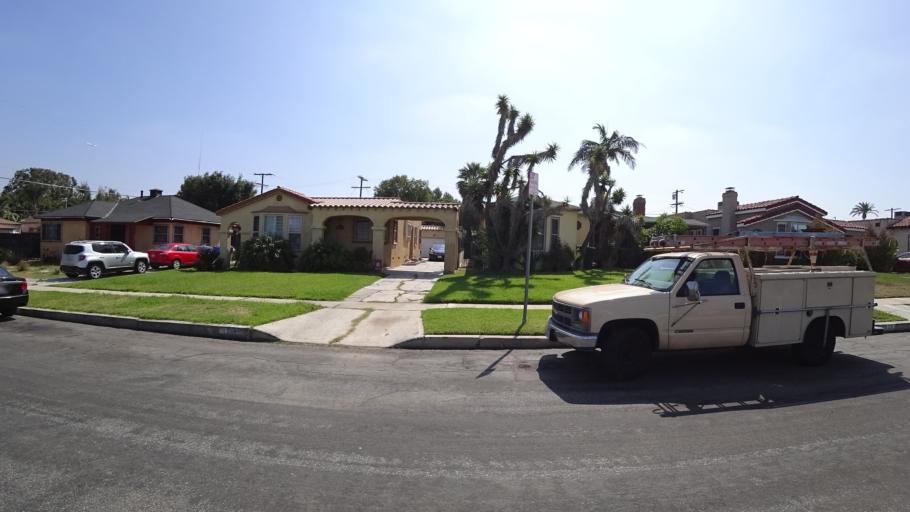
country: US
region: California
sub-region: Los Angeles County
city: Westmont
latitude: 33.9448
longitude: -118.3112
